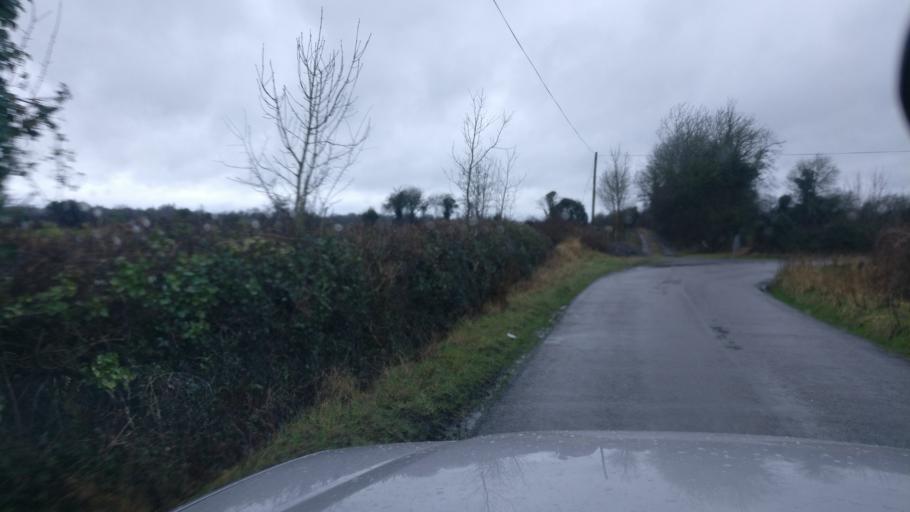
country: IE
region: Connaught
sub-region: County Galway
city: Ballinasloe
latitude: 53.2480
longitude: -8.3568
